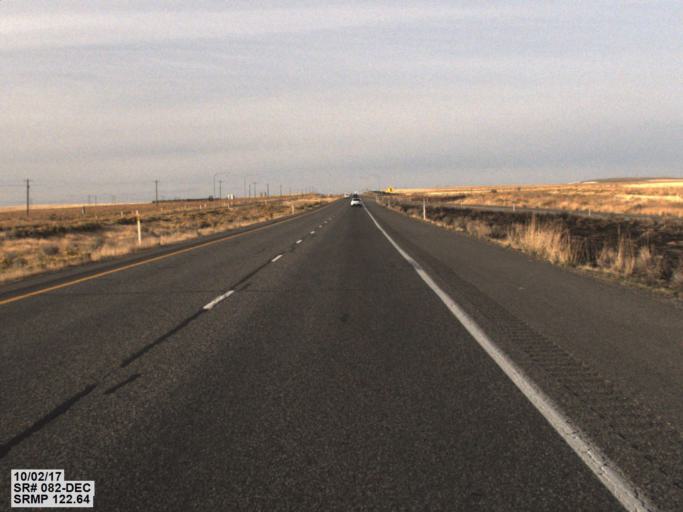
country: US
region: Washington
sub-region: Benton County
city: Highland
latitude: 46.0269
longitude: -119.2246
